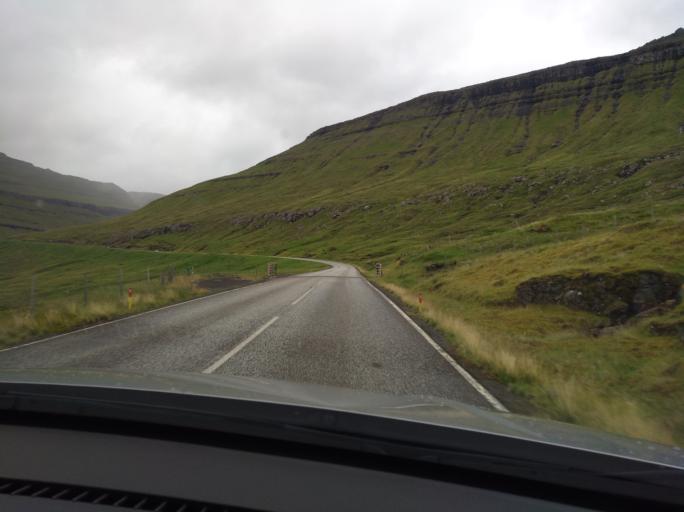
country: FO
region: Eysturoy
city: Fuglafjordur
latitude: 62.2145
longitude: -6.8633
